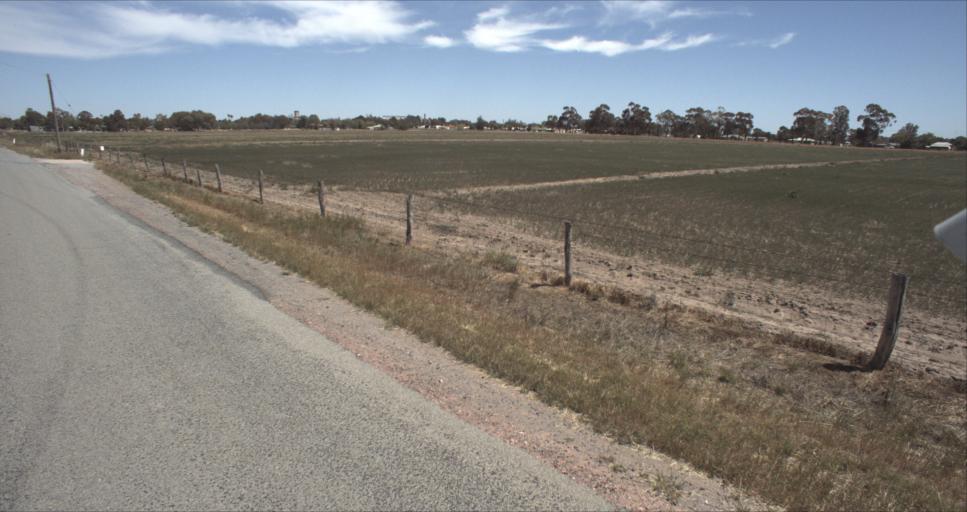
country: AU
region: New South Wales
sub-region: Leeton
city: Leeton
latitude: -34.5962
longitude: 146.4165
